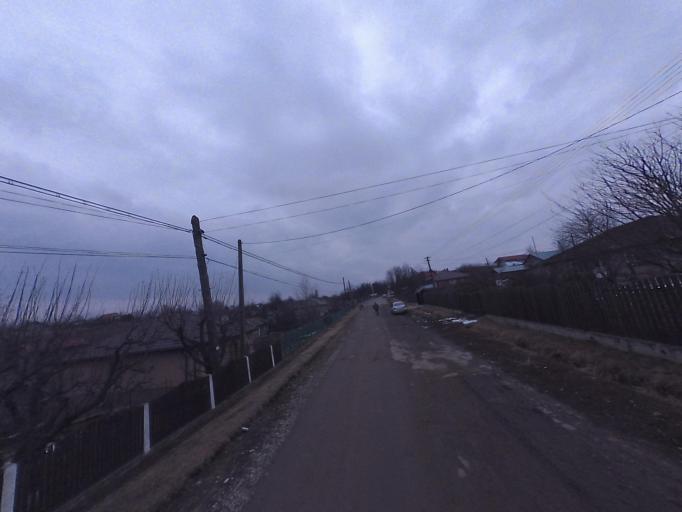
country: RO
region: Iasi
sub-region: Comuna Popricani
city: Popricani
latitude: 47.2896
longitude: 27.5109
